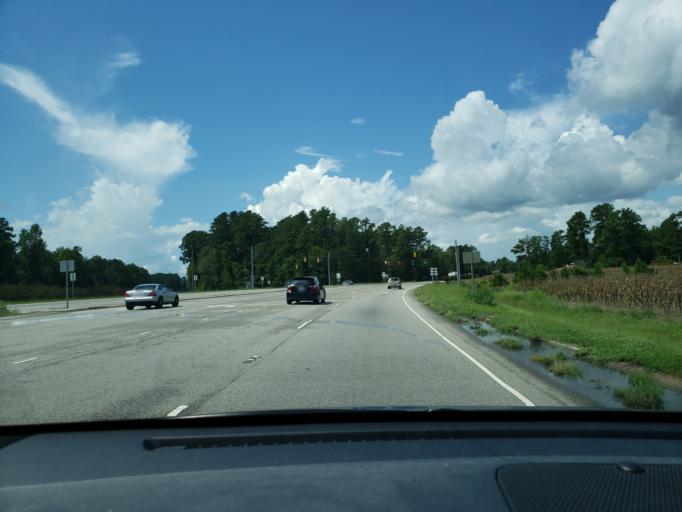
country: US
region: North Carolina
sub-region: Bladen County
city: Elizabethtown
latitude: 34.6457
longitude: -78.7044
